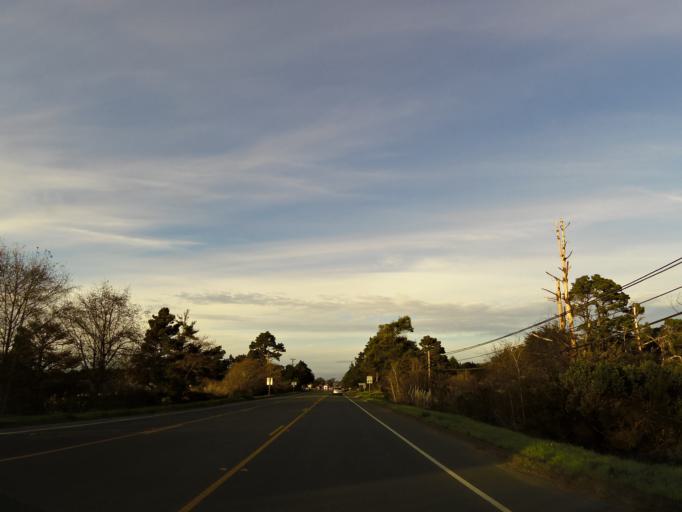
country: US
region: California
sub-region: Mendocino County
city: Fort Bragg
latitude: 39.4055
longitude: -123.8088
